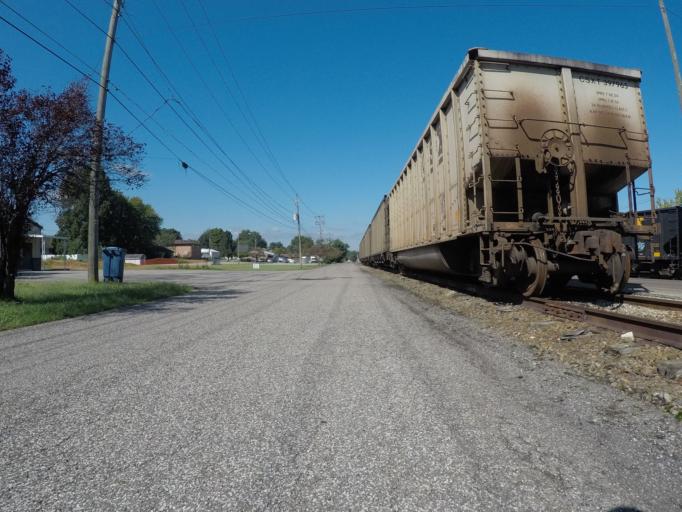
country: US
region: West Virginia
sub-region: Wayne County
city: Ceredo
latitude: 38.3978
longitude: -82.5526
